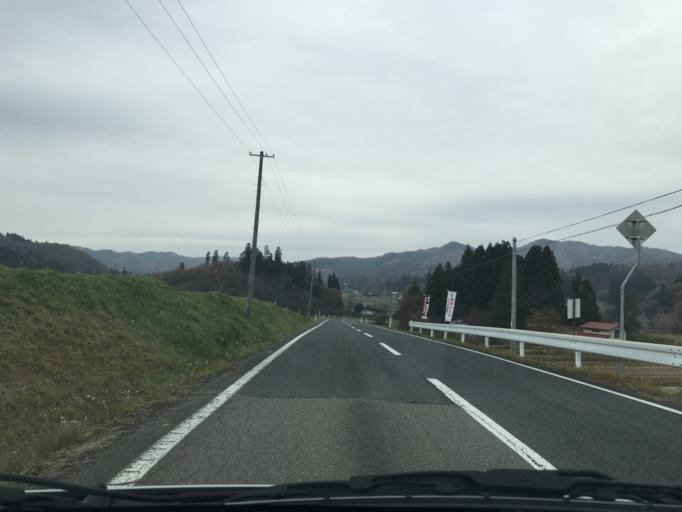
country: JP
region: Iwate
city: Kitakami
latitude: 39.2547
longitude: 141.2069
